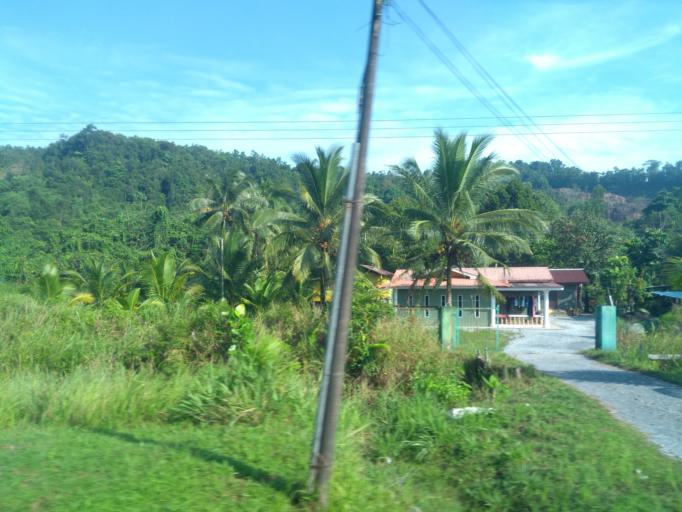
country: MY
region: Sarawak
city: Kuching
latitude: 1.6376
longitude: 110.4534
